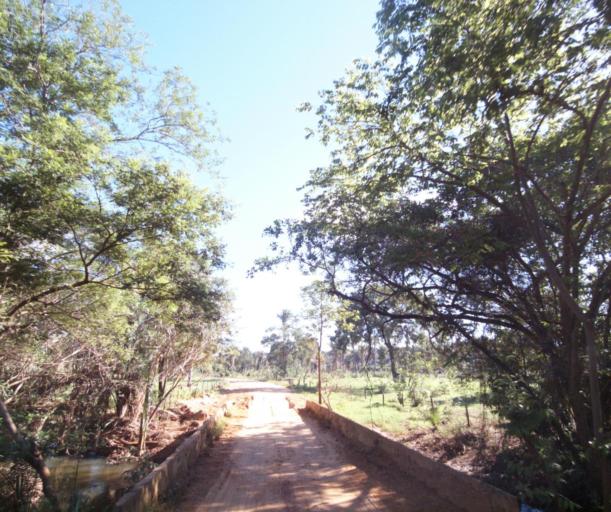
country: BR
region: Bahia
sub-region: Carinhanha
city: Carinhanha
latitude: -14.2386
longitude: -44.5293
